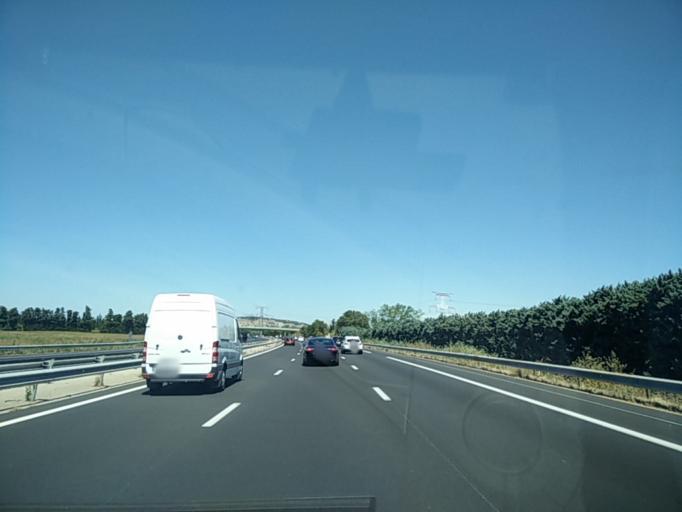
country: FR
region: Provence-Alpes-Cote d'Azur
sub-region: Departement des Bouches-du-Rhone
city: Orgon
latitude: 43.8027
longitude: 5.0400
